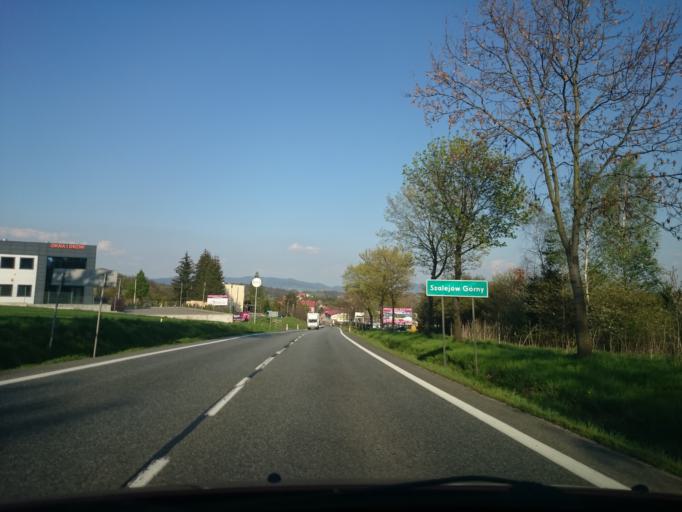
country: PL
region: Lower Silesian Voivodeship
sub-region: Powiat klodzki
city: Polanica-Zdroj
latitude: 50.4266
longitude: 16.5374
